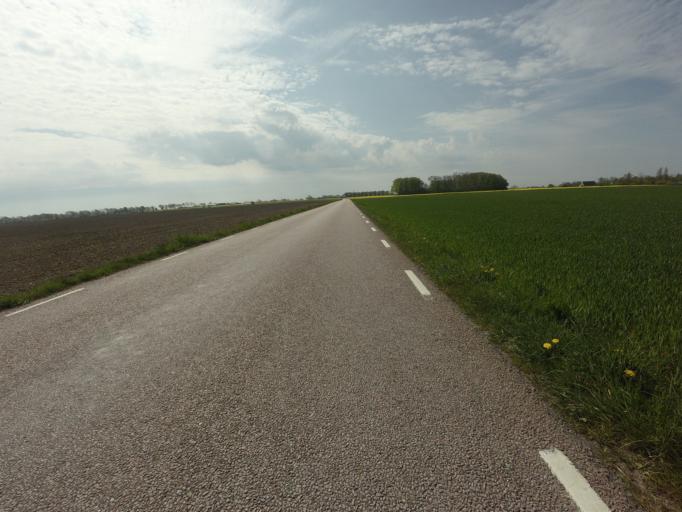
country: SE
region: Skane
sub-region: Hoganas Kommun
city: Hoganas
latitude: 56.2187
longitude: 12.5930
